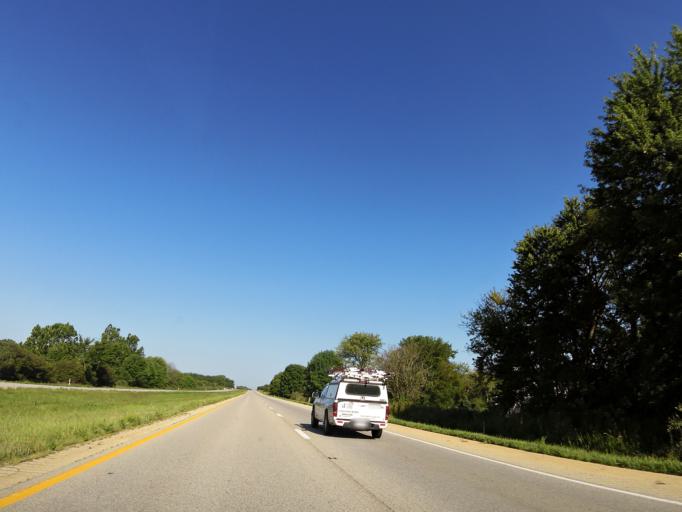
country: US
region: Indiana
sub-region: Boone County
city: Thorntown
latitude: 39.9799
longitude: -86.6783
